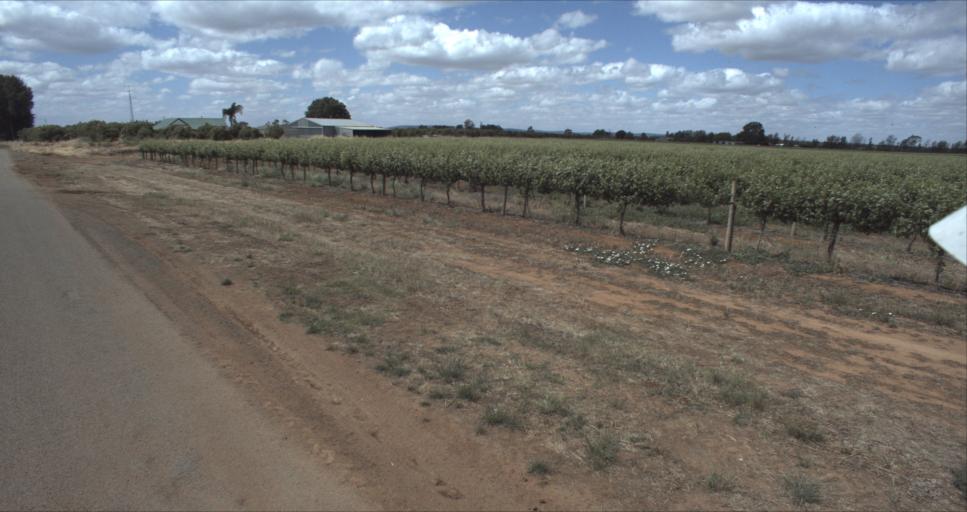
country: AU
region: New South Wales
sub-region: Leeton
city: Leeton
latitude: -34.5861
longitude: 146.3913
